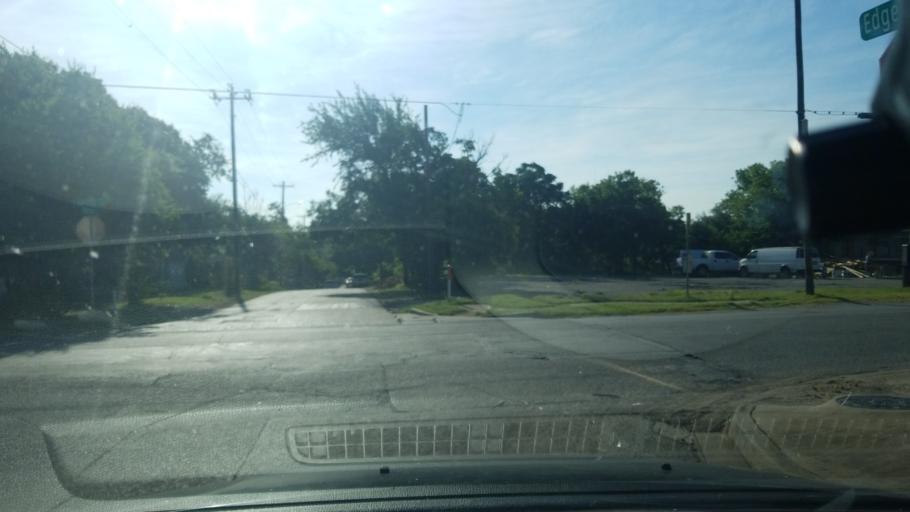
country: US
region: Texas
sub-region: Dallas County
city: Dallas
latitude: 32.7295
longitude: -96.8117
